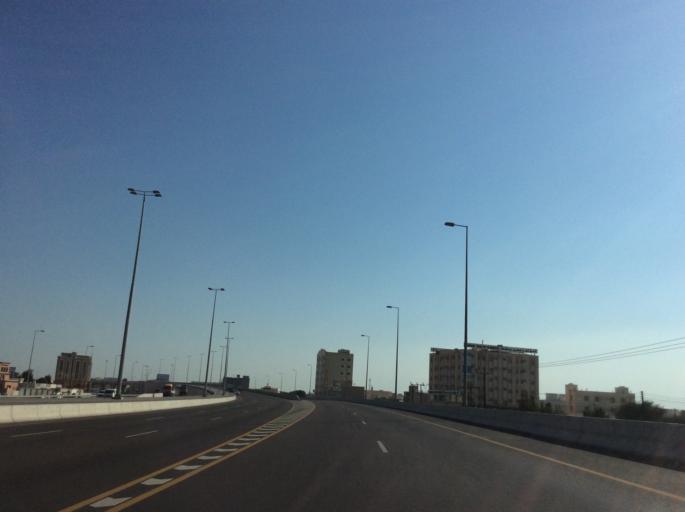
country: OM
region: Al Batinah
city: Al Liwa'
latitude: 24.4304
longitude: 56.6074
